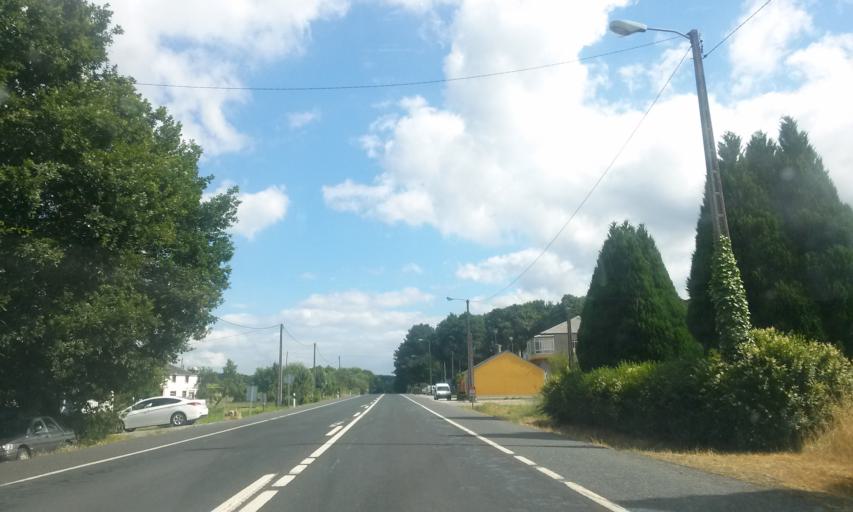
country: ES
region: Galicia
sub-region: Provincia de Lugo
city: Outeiro de Rei
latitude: 43.0973
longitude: -7.6095
